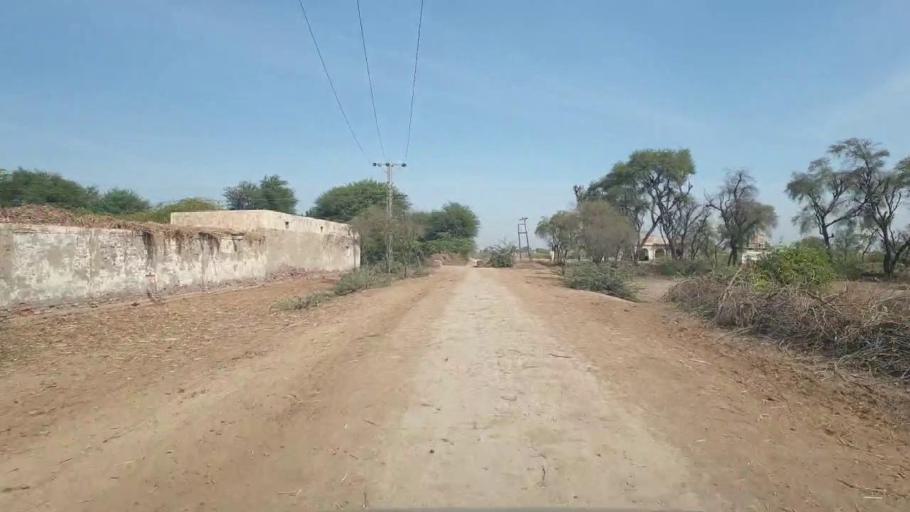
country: PK
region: Sindh
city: Umarkot
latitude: 25.3383
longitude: 69.6230
